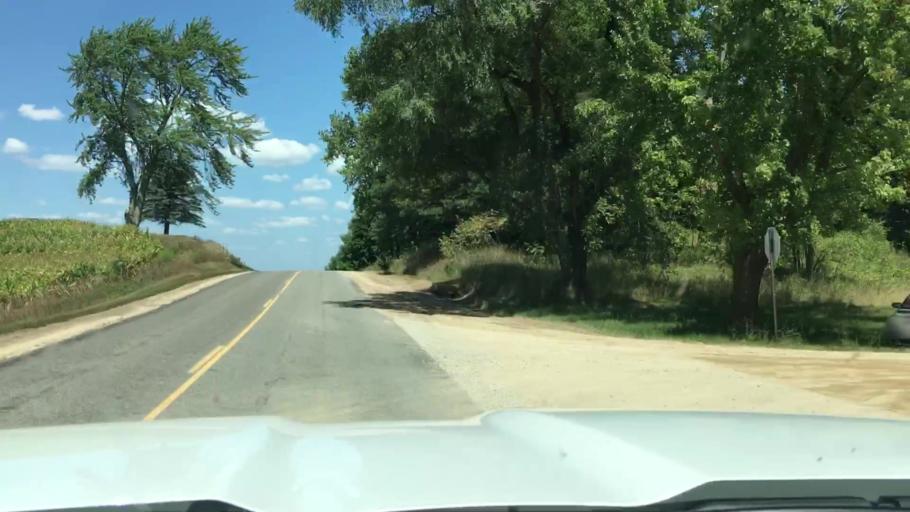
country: US
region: Michigan
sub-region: Muskegon County
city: Ravenna
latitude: 43.2611
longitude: -85.9179
